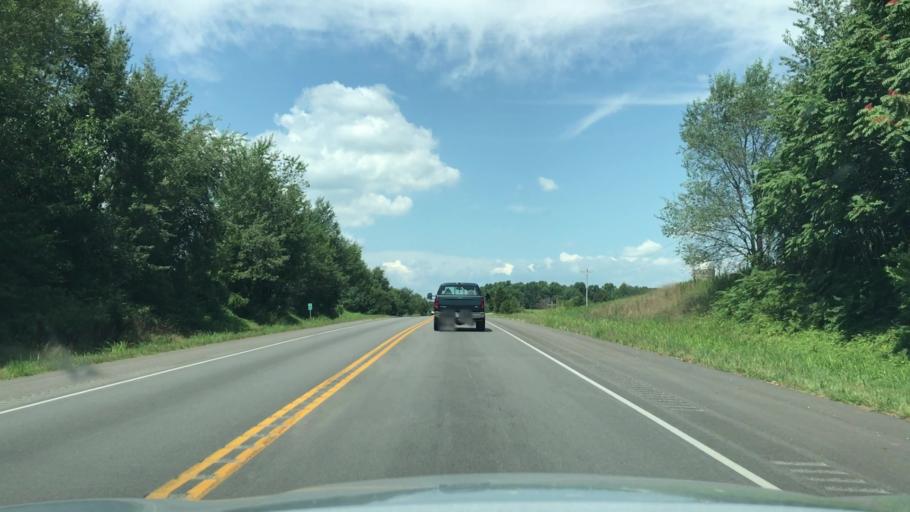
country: US
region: Kentucky
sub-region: Clinton County
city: Albany
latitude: 36.7537
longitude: -85.1229
